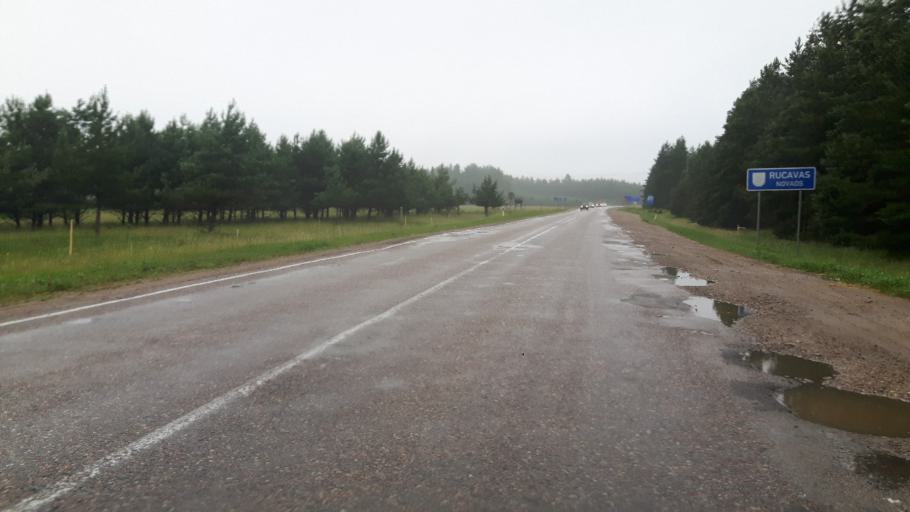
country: LT
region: Klaipedos apskritis
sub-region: Palanga
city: Sventoji
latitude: 56.0790
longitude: 21.1227
